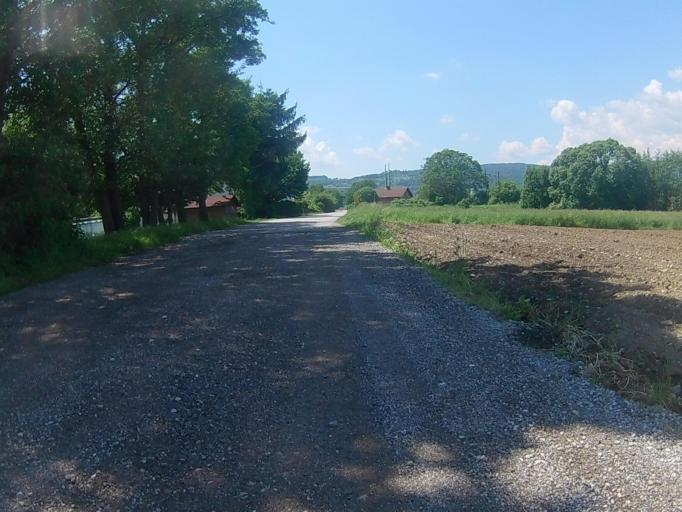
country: SI
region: Hoce-Slivnica
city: Radizel
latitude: 46.4833
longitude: 15.6646
